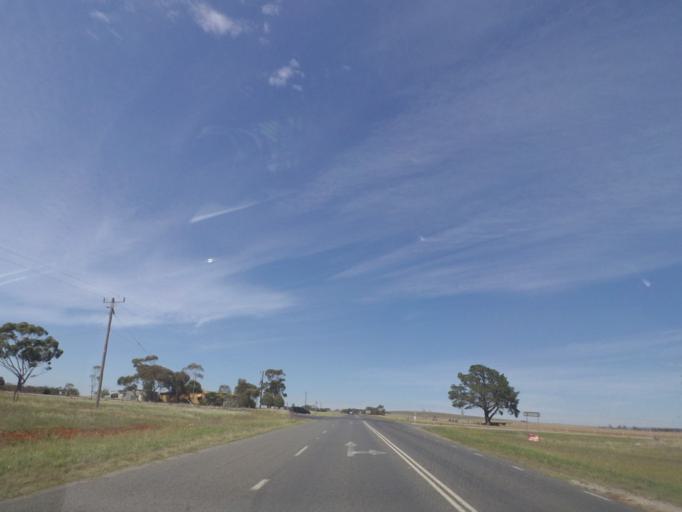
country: AU
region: Victoria
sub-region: Moorabool
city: Bacchus Marsh
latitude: -37.7525
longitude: 144.4435
